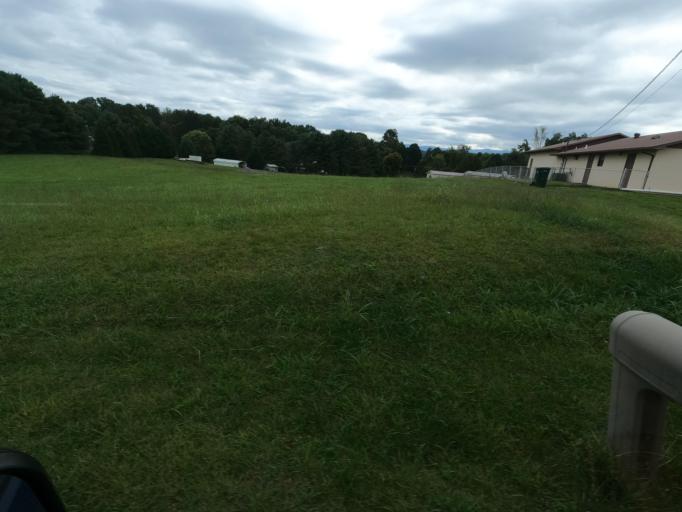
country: US
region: Tennessee
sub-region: Washington County
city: Jonesborough
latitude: 36.2261
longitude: -82.5883
